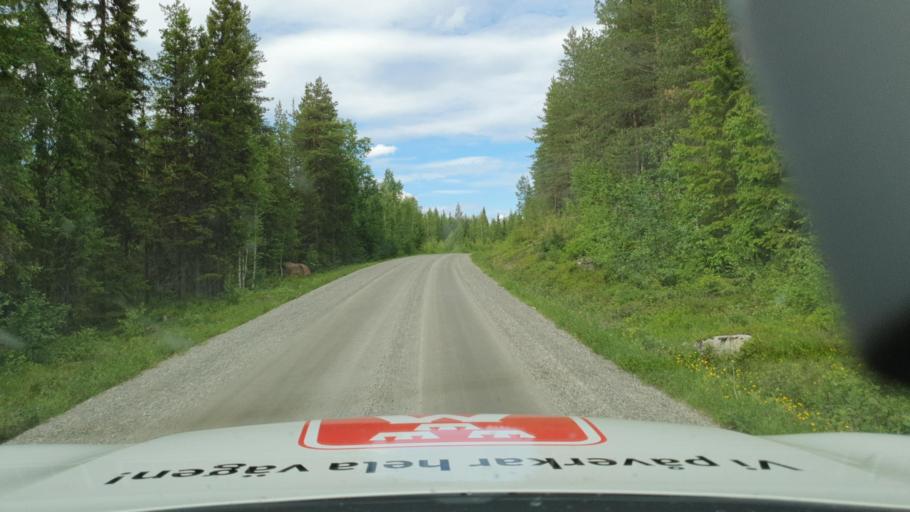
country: SE
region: Vaesterbotten
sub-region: Norsjo Kommun
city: Norsjoe
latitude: 64.8341
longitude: 19.7025
